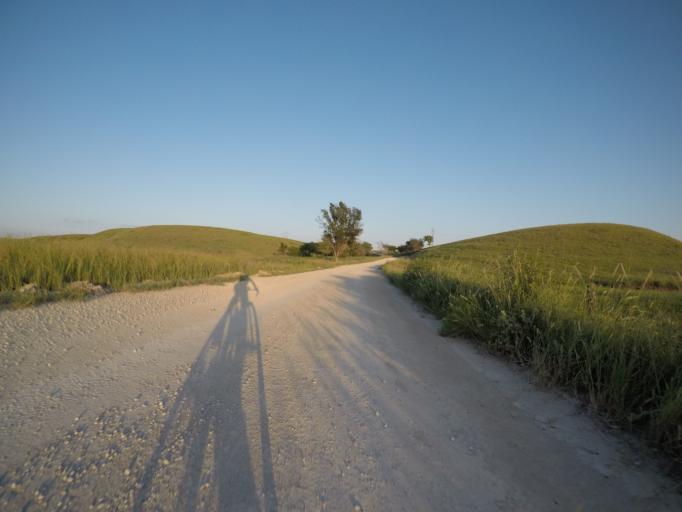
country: US
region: Kansas
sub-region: Riley County
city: Ogden
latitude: 39.0102
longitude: -96.6434
